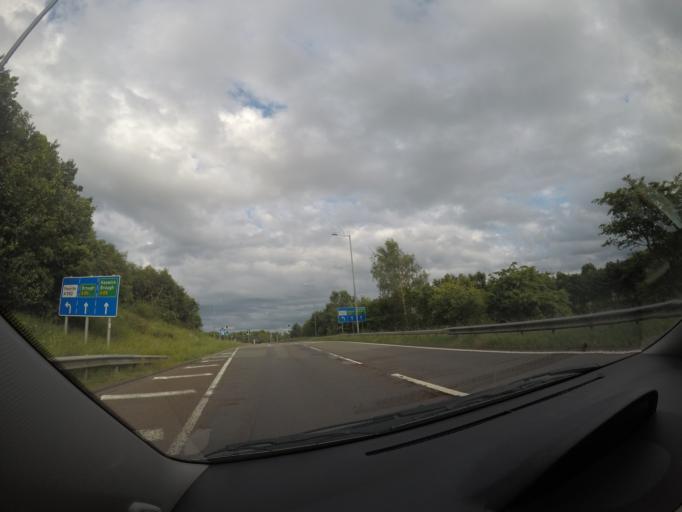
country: GB
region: England
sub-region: Cumbria
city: Penrith
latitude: 54.6543
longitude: -2.7617
